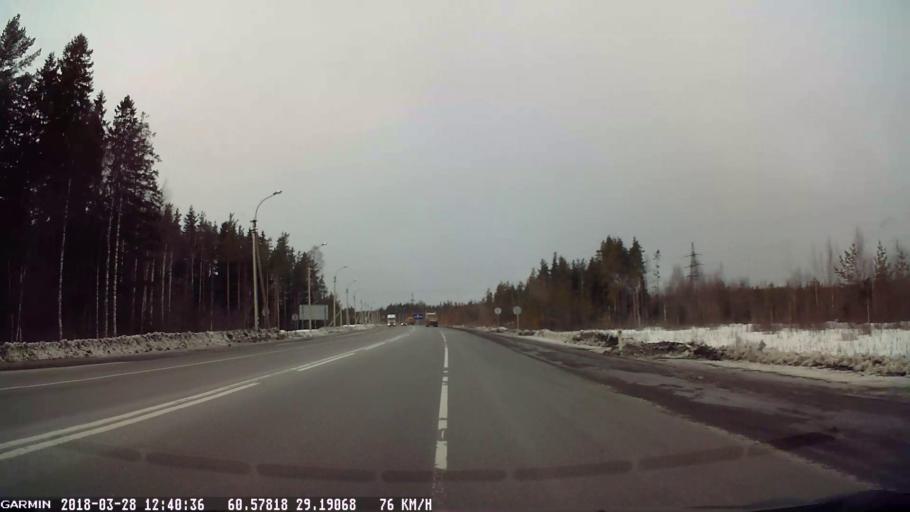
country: RU
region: Leningrad
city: Veshchevo
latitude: 60.5783
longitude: 29.1904
